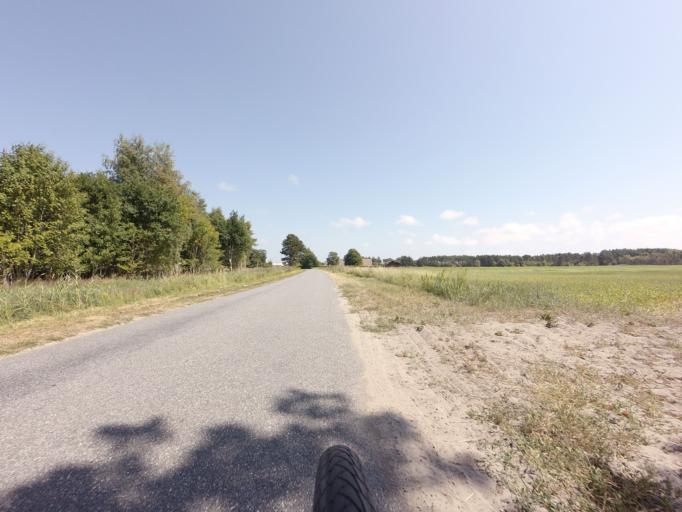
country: DK
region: North Denmark
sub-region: Laeso Kommune
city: Byrum
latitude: 57.2519
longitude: 10.9609
